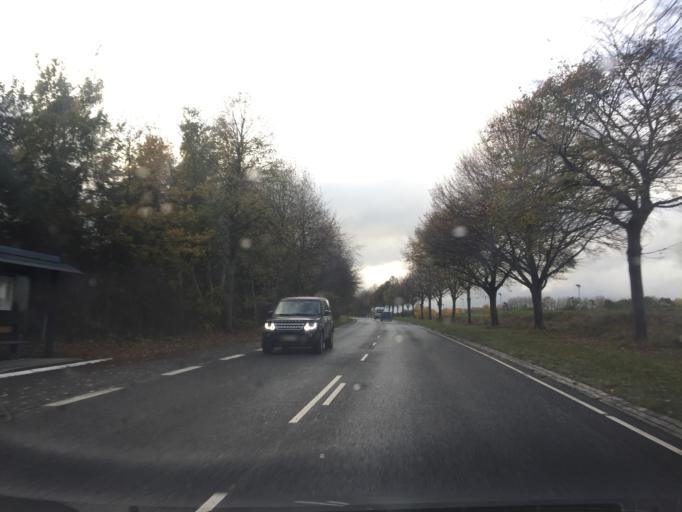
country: DK
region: Capital Region
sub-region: Fredensborg Kommune
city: Humlebaek
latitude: 55.9666
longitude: 12.5116
